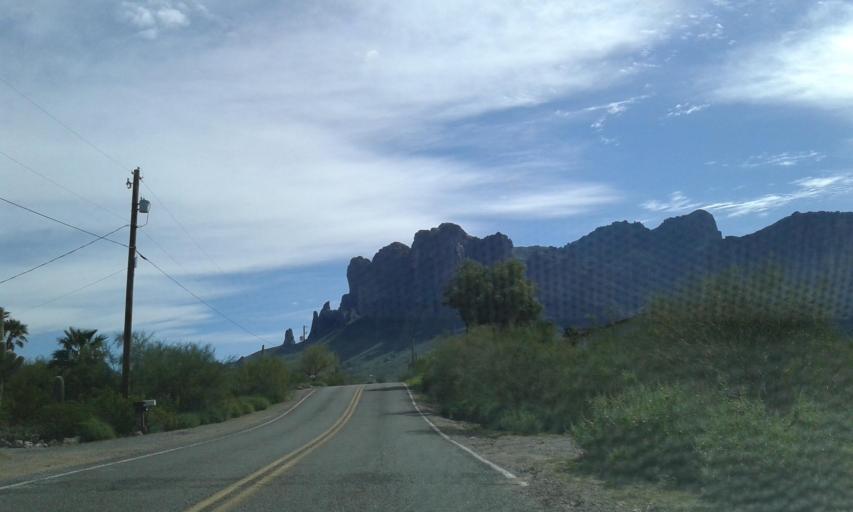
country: US
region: Arizona
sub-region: Pinal County
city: Apache Junction
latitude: 33.4496
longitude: -111.4891
